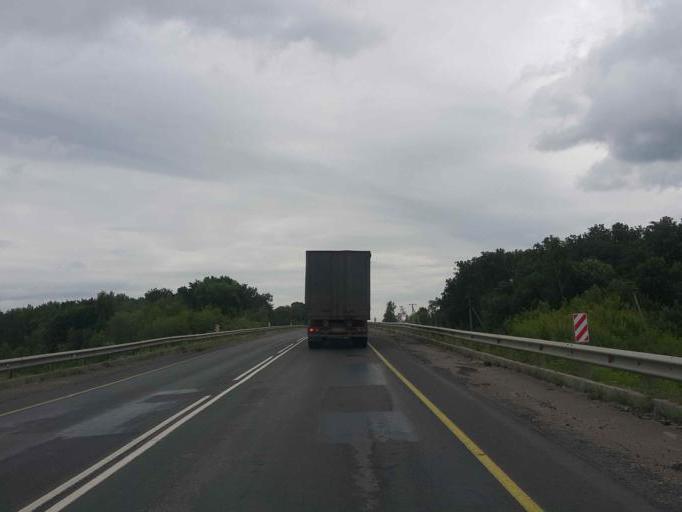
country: RU
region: Tambov
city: Zavoronezhskoye
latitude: 52.9191
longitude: 40.6238
